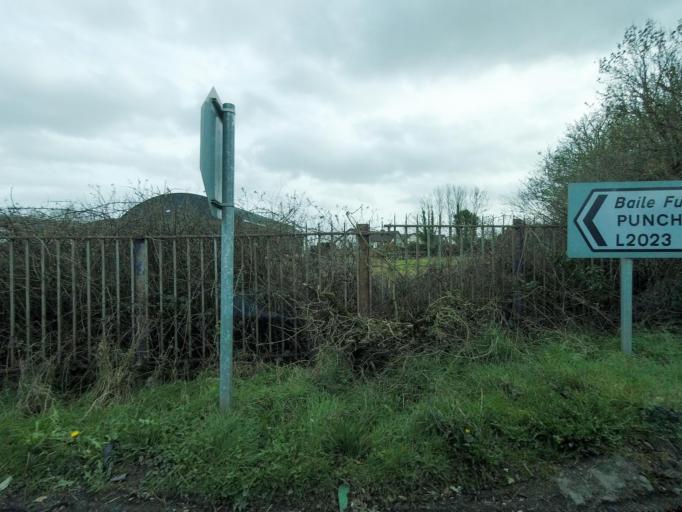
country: IE
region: Leinster
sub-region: Kildare
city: Naas
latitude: 53.1734
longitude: -6.6856
